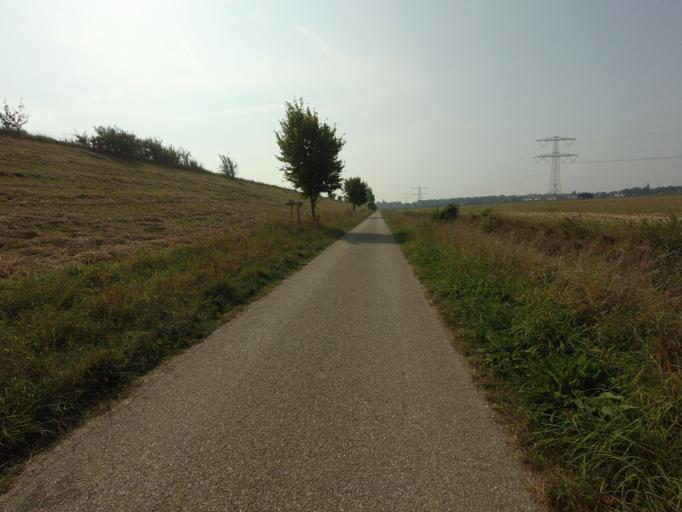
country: BE
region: Flanders
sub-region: Provincie Limburg
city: Maaseik
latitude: 51.0866
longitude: 5.8307
